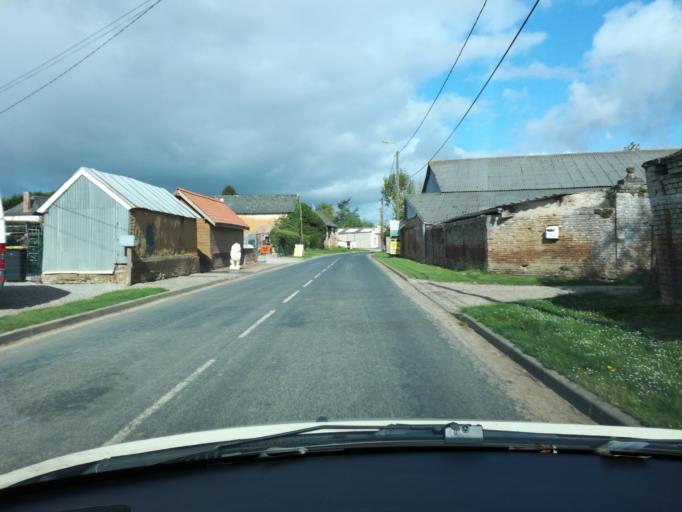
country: FR
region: Picardie
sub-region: Departement de la Somme
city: Beaucamps-le-Vieux
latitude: 49.8675
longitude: 1.8375
